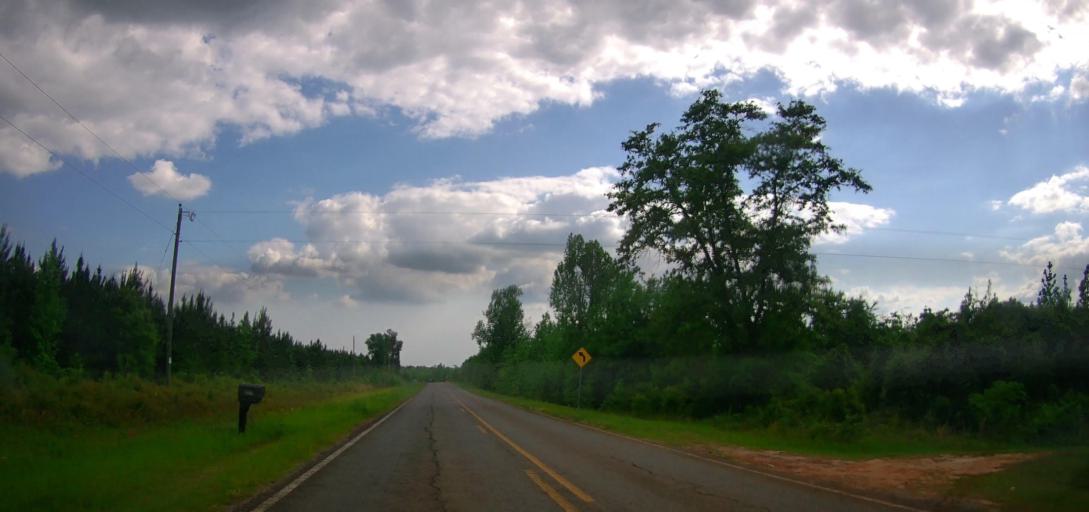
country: US
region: Georgia
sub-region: Washington County
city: Tennille
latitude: 32.7678
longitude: -82.9300
